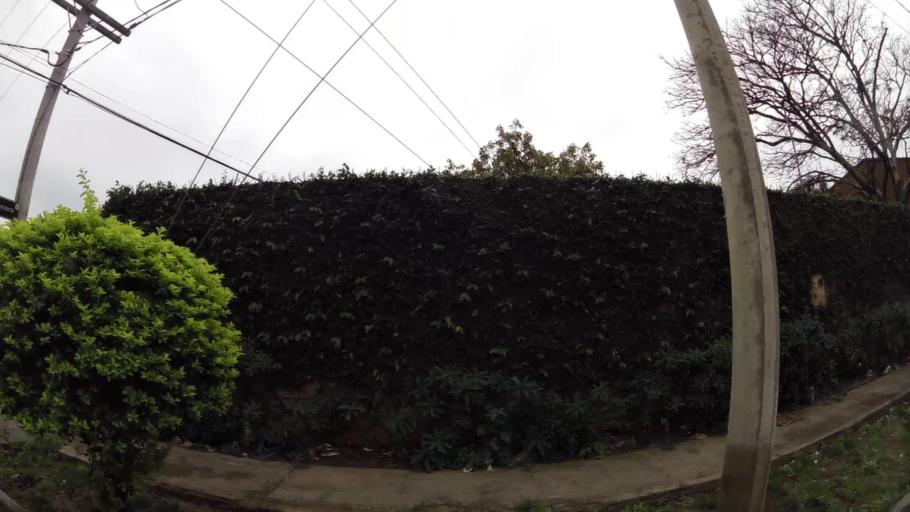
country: BO
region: Santa Cruz
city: Santa Cruz de la Sierra
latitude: -17.7569
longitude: -63.1778
